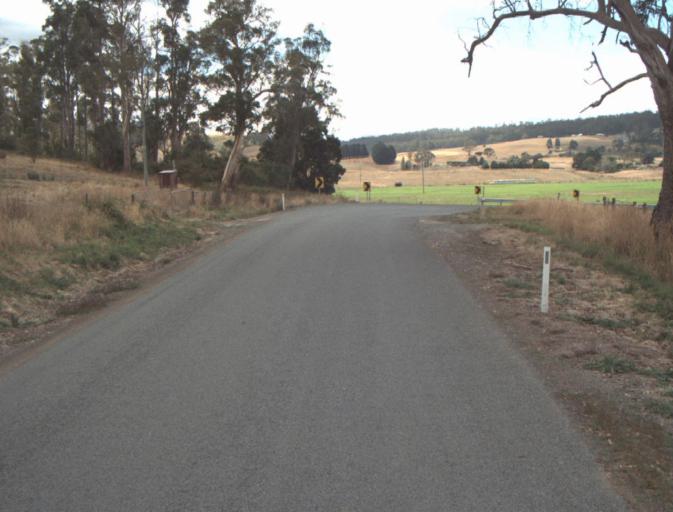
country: AU
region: Tasmania
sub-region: Launceston
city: Mayfield
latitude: -41.2370
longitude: 147.1972
